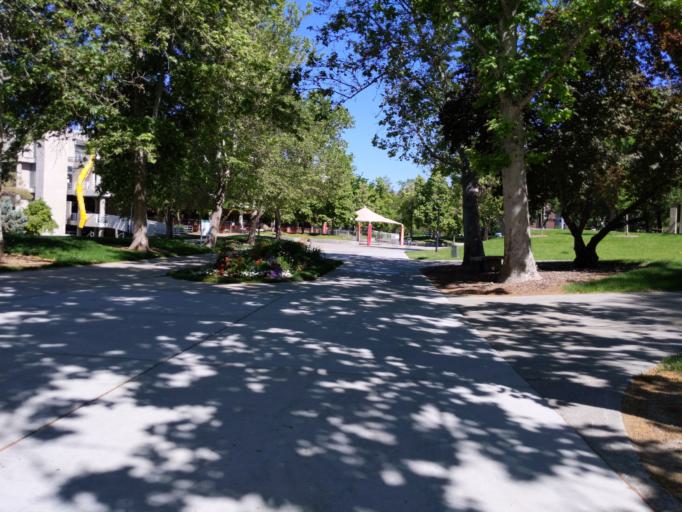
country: US
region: Utah
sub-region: Salt Lake County
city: Salt Lake City
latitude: 40.7645
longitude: -111.8471
